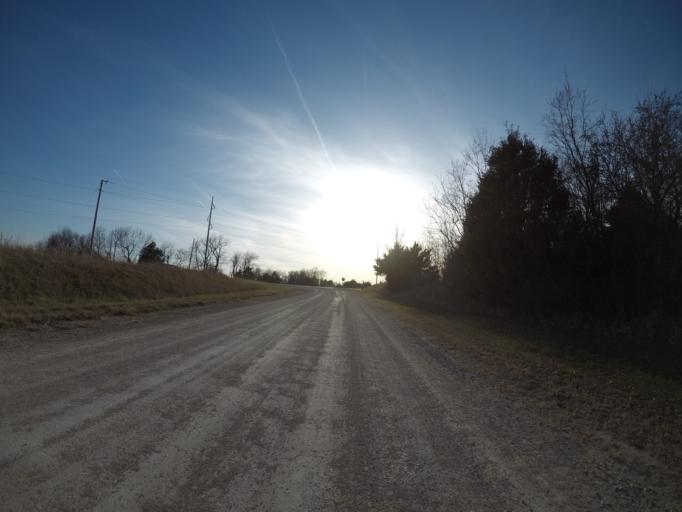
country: US
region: Kansas
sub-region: Riley County
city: Manhattan
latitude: 39.2545
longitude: -96.6716
